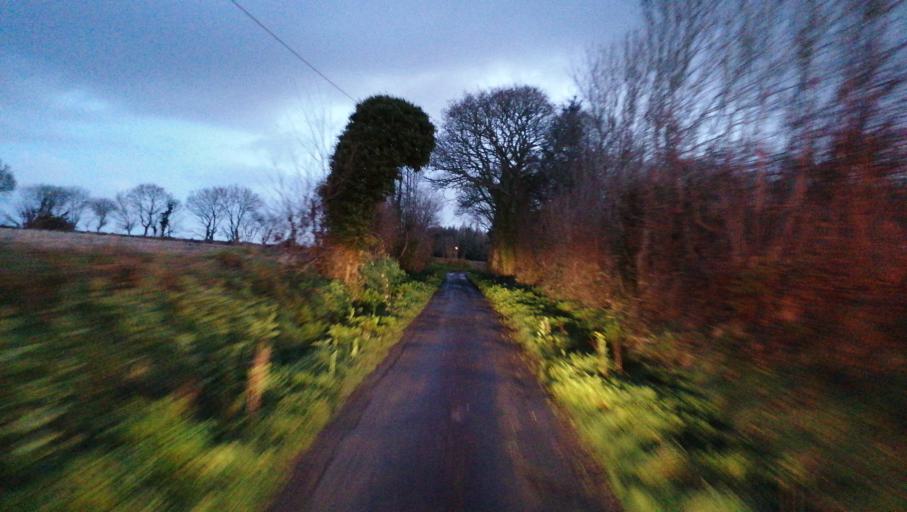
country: FR
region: Brittany
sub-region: Departement des Cotes-d'Armor
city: Plouha
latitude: 48.6683
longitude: -2.9654
